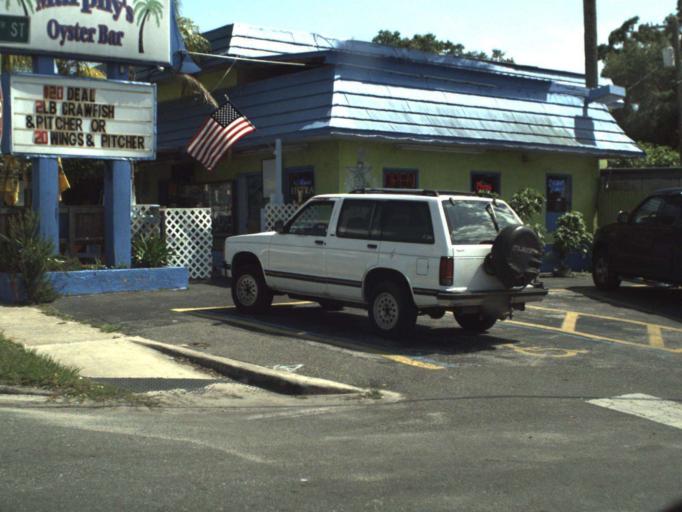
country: US
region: Florida
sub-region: Marion County
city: Ocala
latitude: 29.1688
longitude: -82.1387
